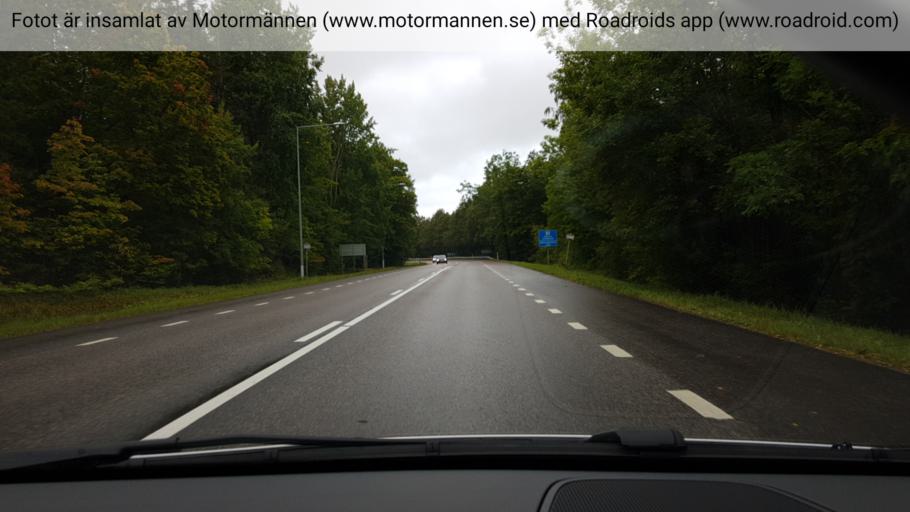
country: SE
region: Uppsala
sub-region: Alvkarleby Kommun
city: Skutskaer
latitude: 60.6465
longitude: 17.3735
